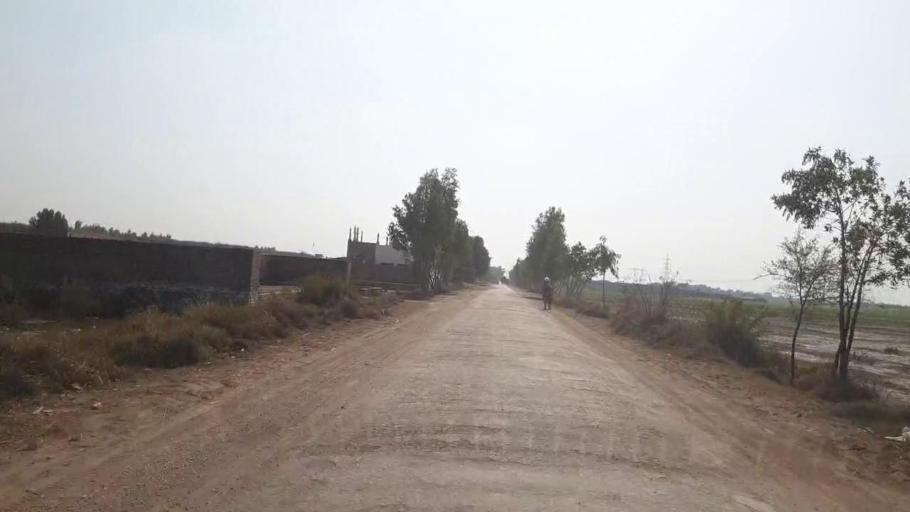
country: PK
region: Sindh
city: Bhit Shah
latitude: 25.6999
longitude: 68.5436
